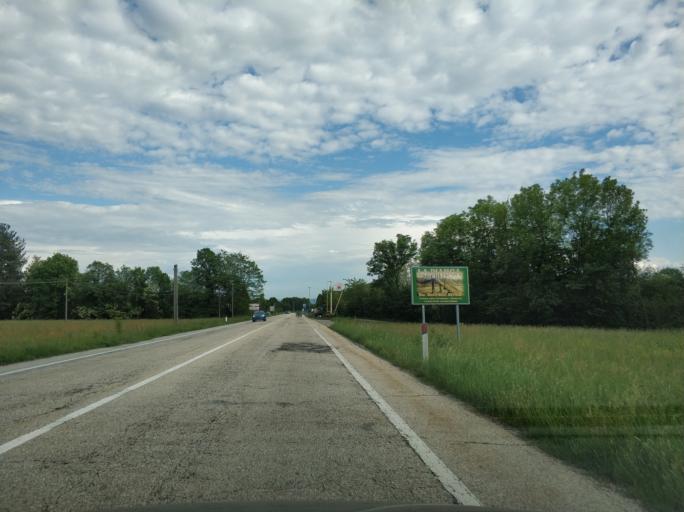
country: IT
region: Piedmont
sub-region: Provincia di Torino
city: Fiano
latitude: 45.2169
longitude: 7.5403
